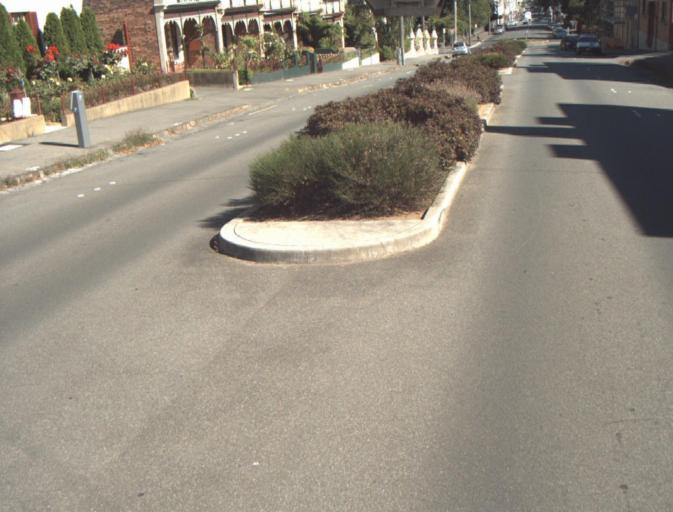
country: AU
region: Tasmania
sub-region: Launceston
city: Launceston
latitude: -41.4416
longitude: 147.1422
